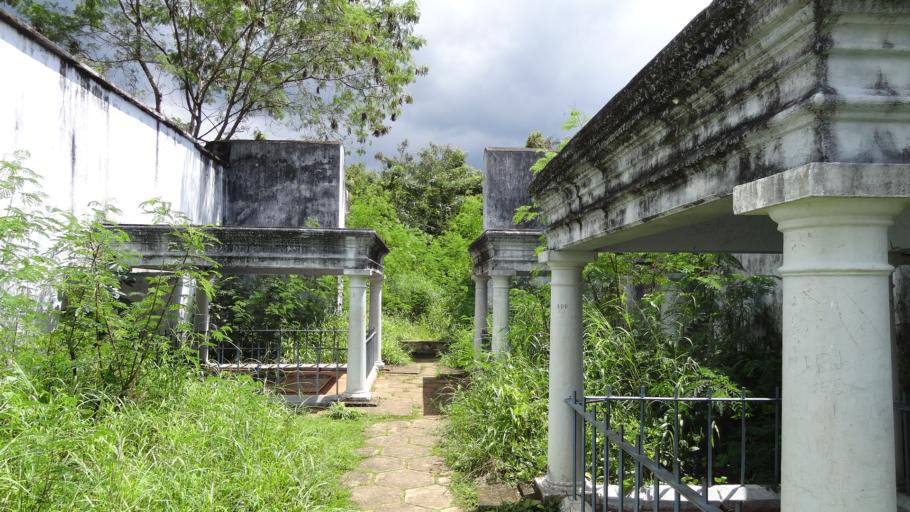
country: IN
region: Tamil Nadu
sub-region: Kanniyakumari
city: Padmanabhapuram
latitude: 8.2401
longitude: 77.3381
